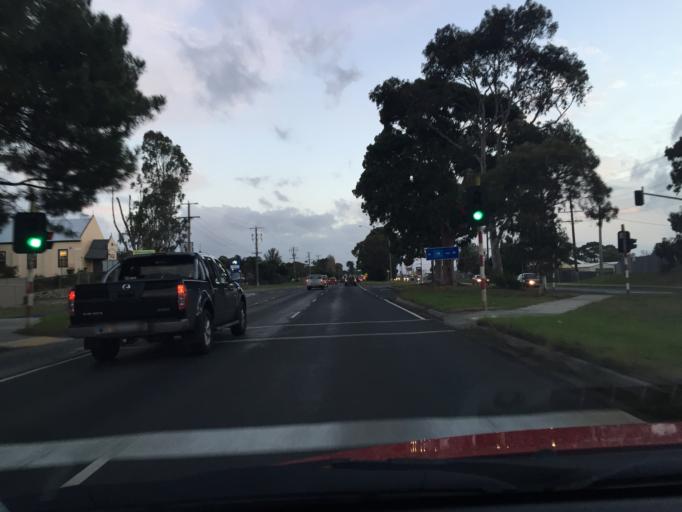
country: AU
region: Victoria
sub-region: Frankston
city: Carrum Downs
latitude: -38.0915
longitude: 145.1792
